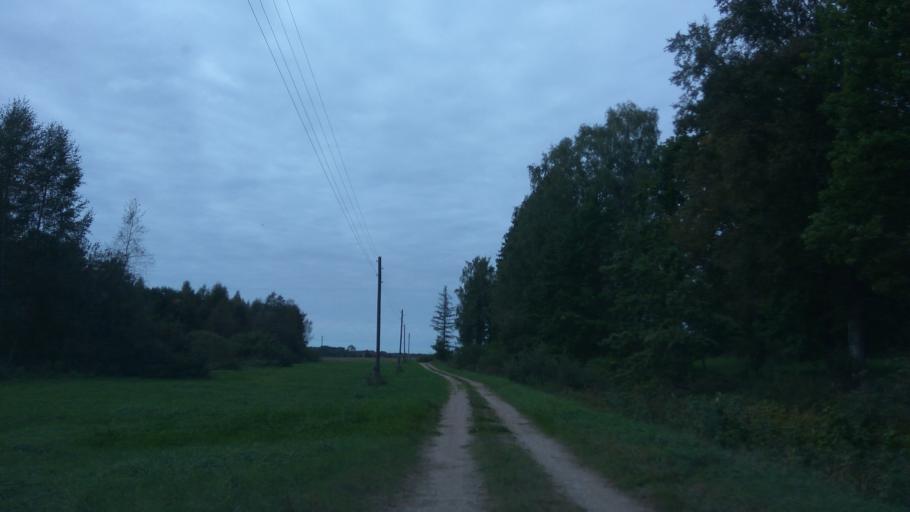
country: LV
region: Kuldigas Rajons
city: Kuldiga
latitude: 57.2410
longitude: 21.9637
